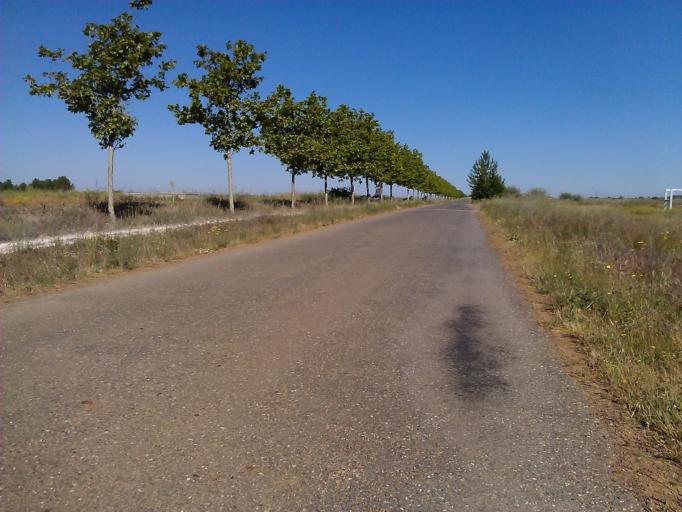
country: ES
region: Castille and Leon
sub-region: Provincia de Leon
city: Bercianos del Real Camino
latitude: 42.4003
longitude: -5.1727
